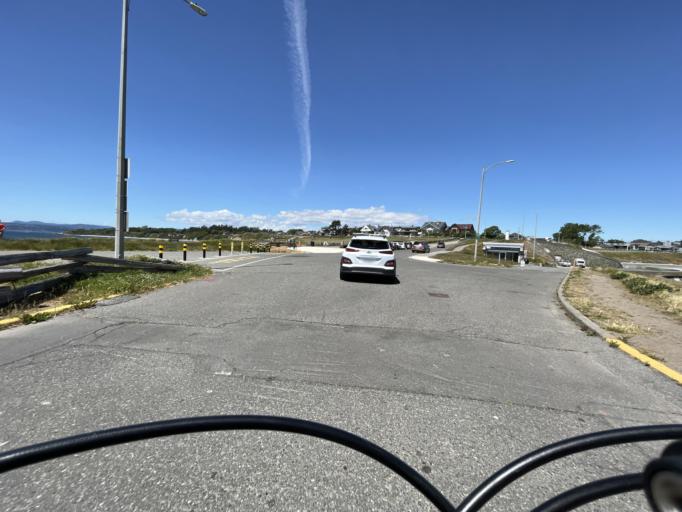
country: CA
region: British Columbia
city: Victoria
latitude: 48.4043
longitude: -123.3494
